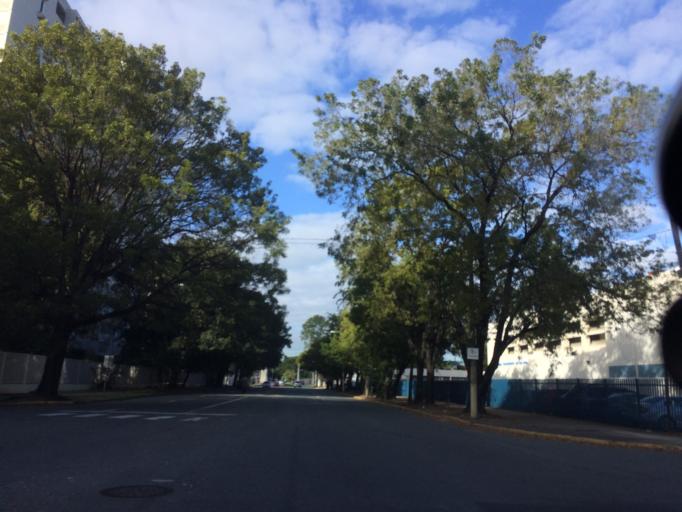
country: PR
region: Catano
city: Catano
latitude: 18.4282
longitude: -66.0658
